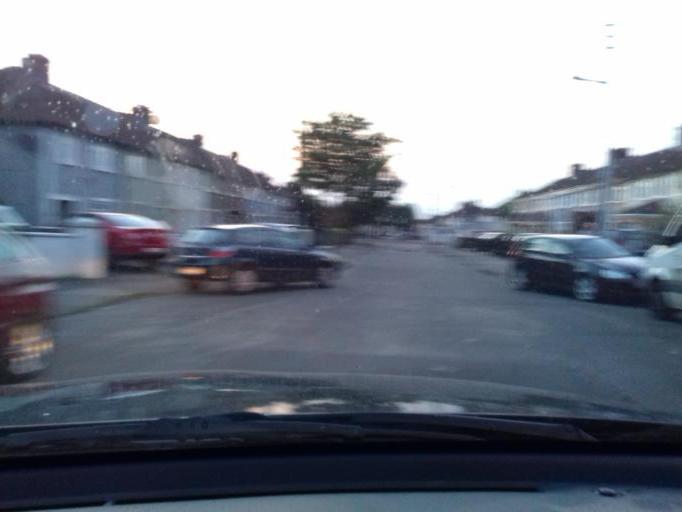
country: IE
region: Leinster
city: Crumlin
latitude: 53.3284
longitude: -6.3264
